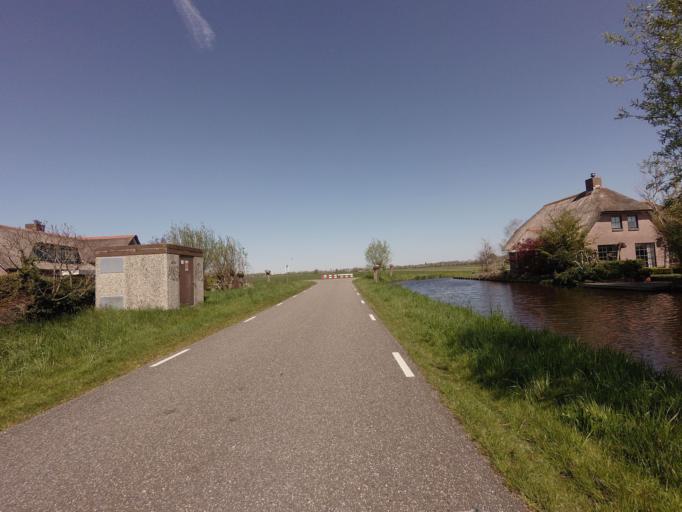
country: NL
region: South Holland
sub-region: Gemeente Boskoop
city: Boskoop
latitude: 52.0981
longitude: 4.6593
